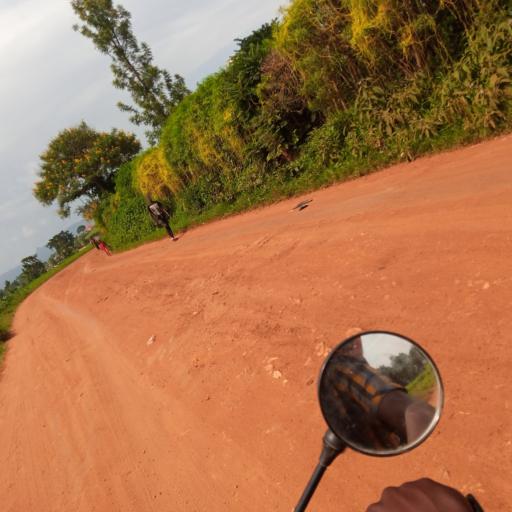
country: UG
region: Eastern Region
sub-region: Mbale District
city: Mbale
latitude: 1.0943
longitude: 34.1879
